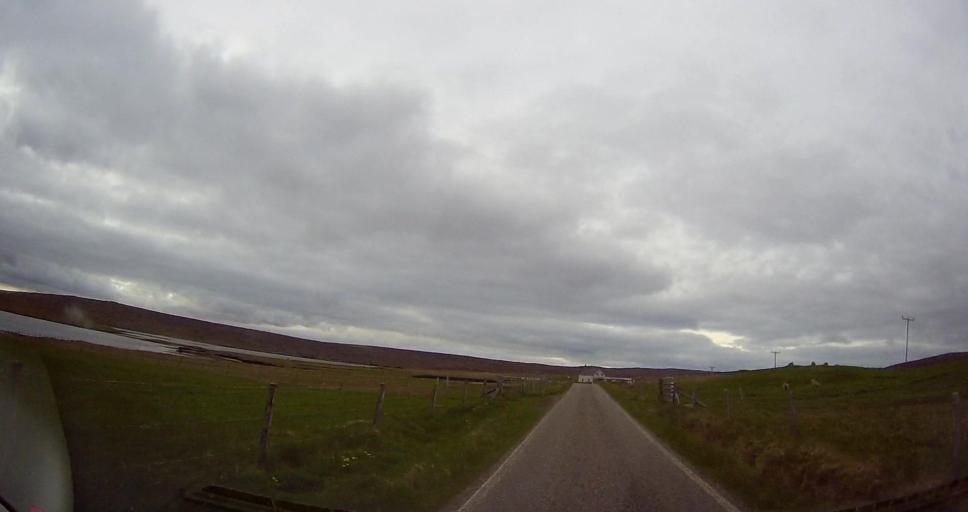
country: GB
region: Scotland
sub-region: Shetland Islands
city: Shetland
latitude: 60.5020
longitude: -1.0950
